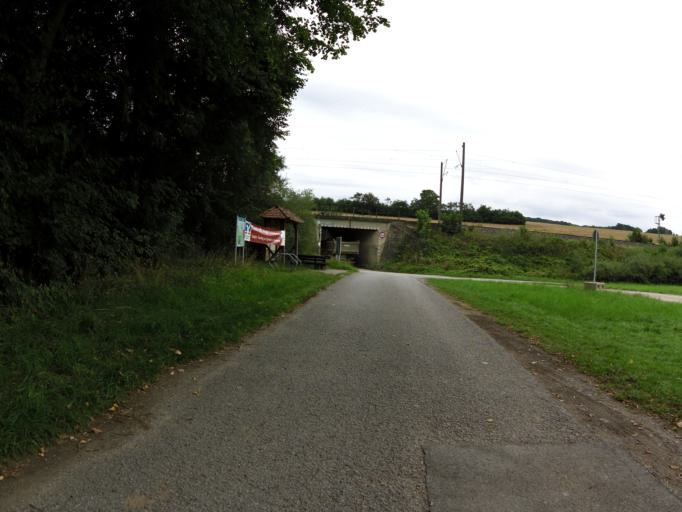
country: DE
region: Bavaria
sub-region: Regierungsbezirk Unterfranken
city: Wonfurt
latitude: 50.0193
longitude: 10.4599
